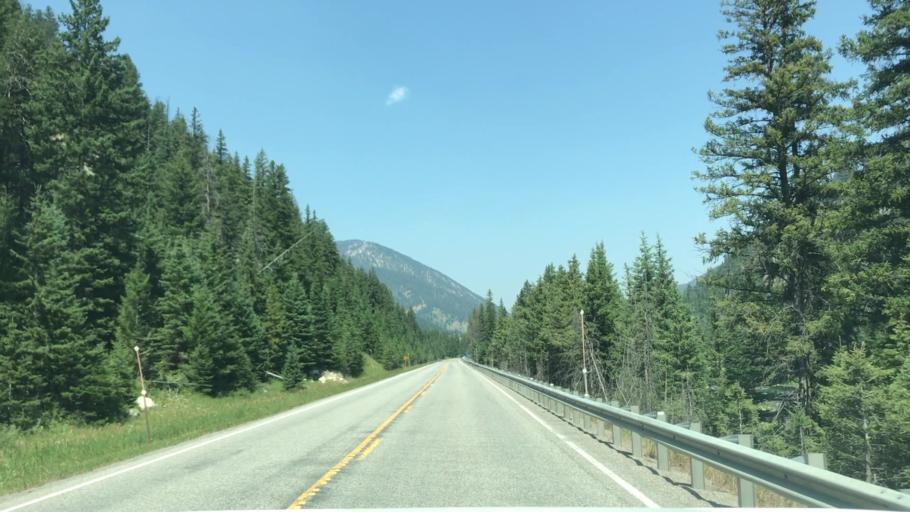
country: US
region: Montana
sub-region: Gallatin County
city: Big Sky
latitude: 45.0847
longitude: -111.2097
